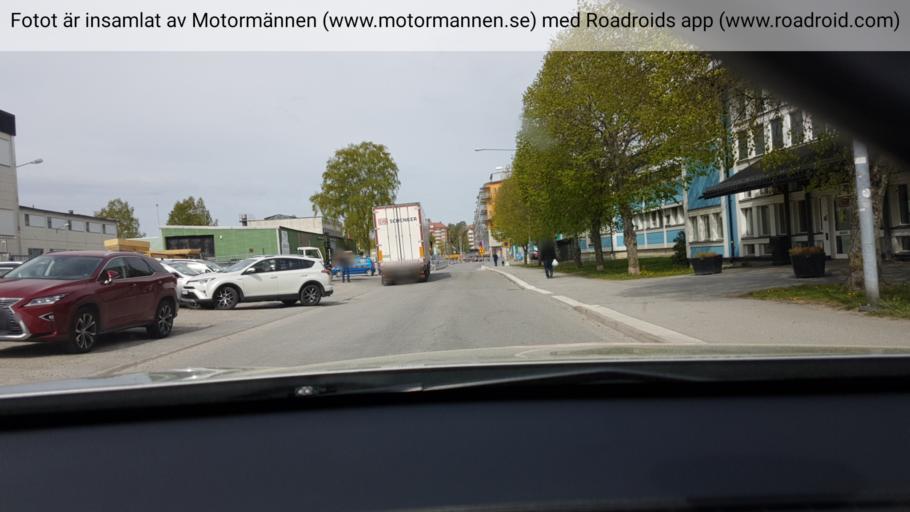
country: SE
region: Stockholm
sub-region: Huddinge Kommun
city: Huddinge
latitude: 59.2312
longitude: 17.9933
